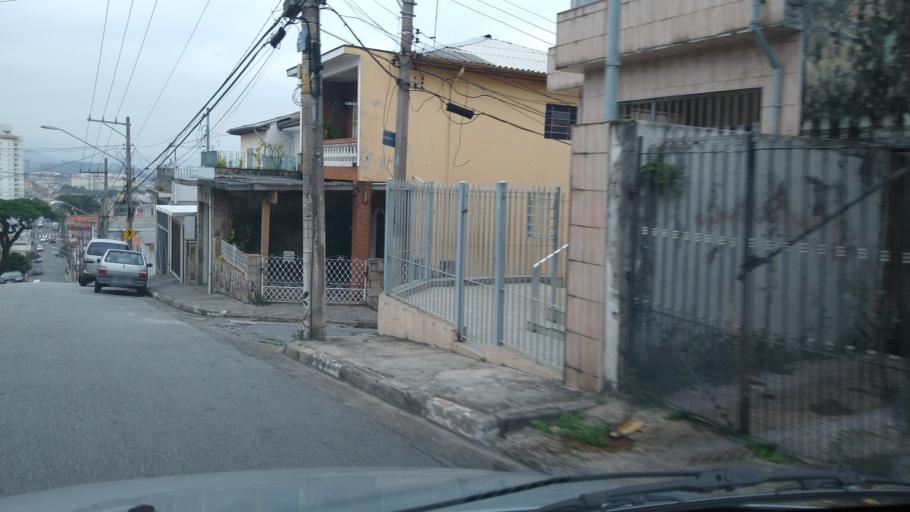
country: BR
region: Sao Paulo
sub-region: Guarulhos
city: Guarulhos
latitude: -23.4850
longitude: -46.5893
